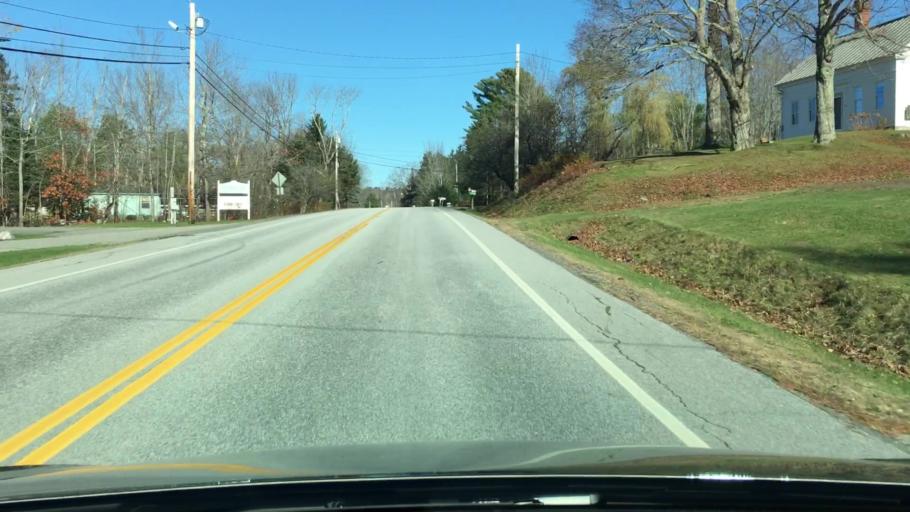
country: US
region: Maine
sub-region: Waldo County
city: Winterport
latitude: 44.6498
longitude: -68.8241
